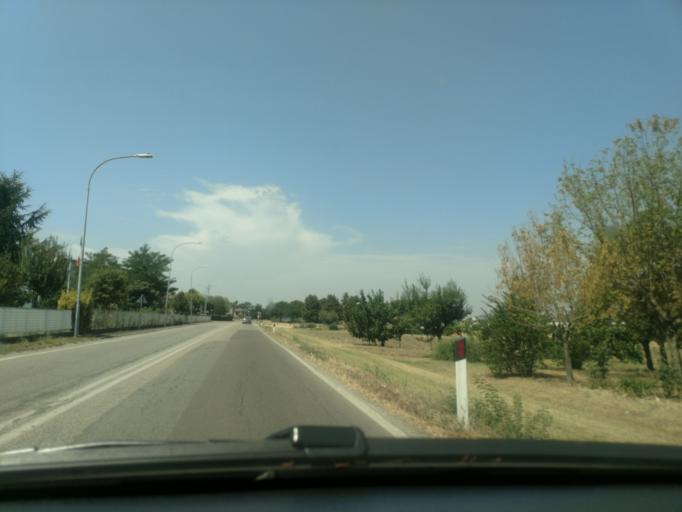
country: IT
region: Emilia-Romagna
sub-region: Provincia di Bologna
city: Medicina-Buda
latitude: 44.4402
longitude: 11.6181
